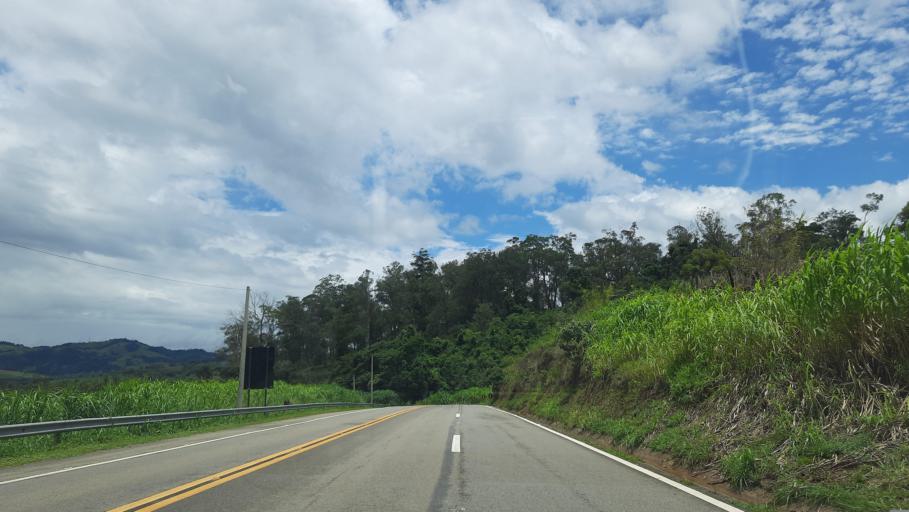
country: BR
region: Sao Paulo
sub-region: Vargem Grande Do Sul
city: Vargem Grande do Sul
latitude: -21.7994
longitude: -46.8168
